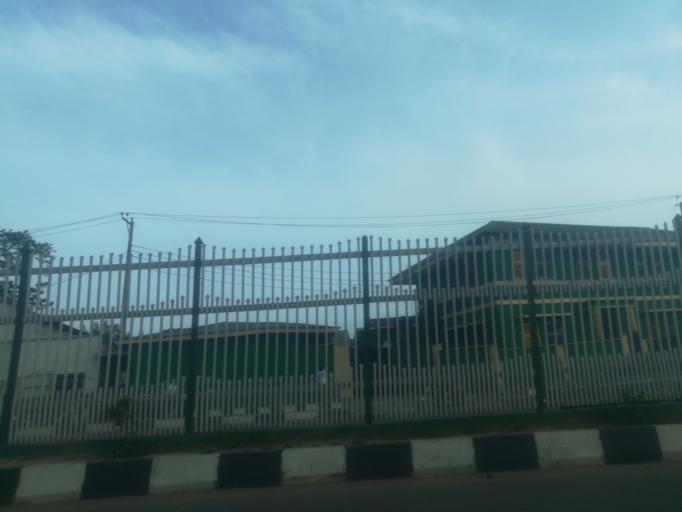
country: NG
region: Ogun
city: Abeokuta
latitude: 7.1363
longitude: 3.3324
